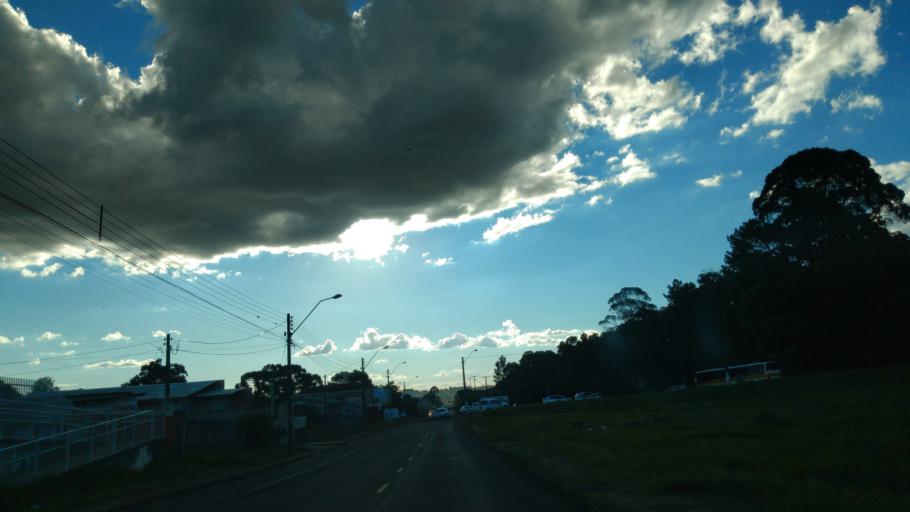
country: BR
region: Parana
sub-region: Guarapuava
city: Guarapuava
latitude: -25.3944
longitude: -51.4810
